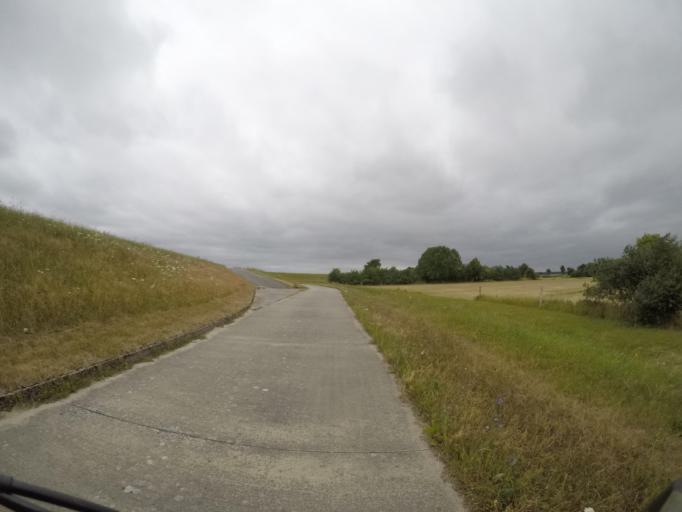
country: DE
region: Lower Saxony
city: Hitzacker
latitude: 53.1567
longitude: 11.0705
